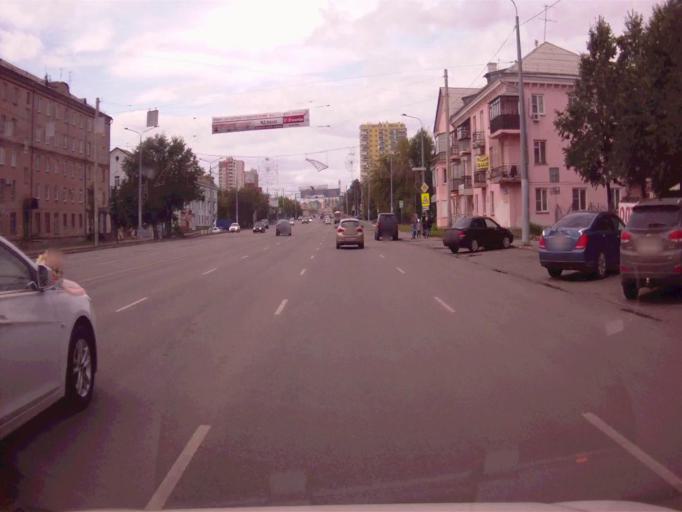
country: RU
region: Chelyabinsk
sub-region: Gorod Chelyabinsk
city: Chelyabinsk
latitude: 55.1421
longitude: 61.3923
